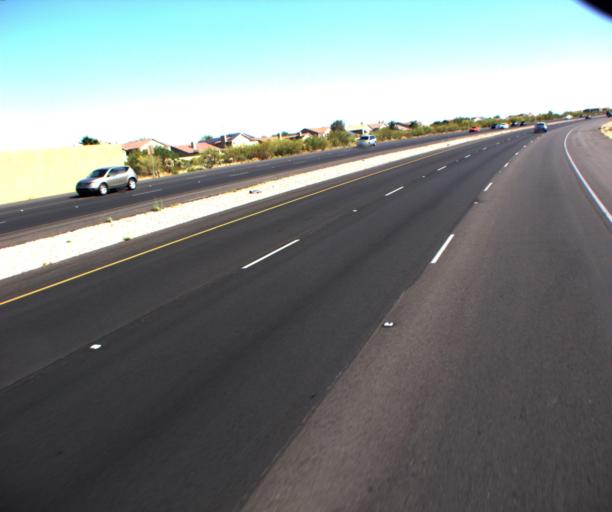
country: US
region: Arizona
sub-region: Pima County
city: Catalina
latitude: 32.4493
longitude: -110.9336
